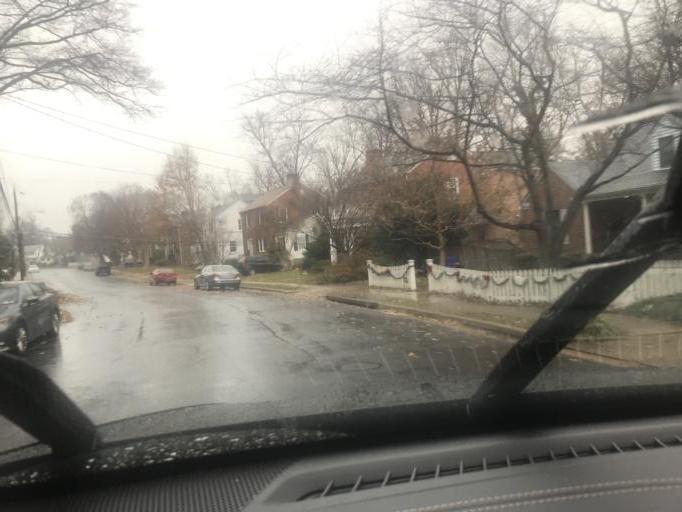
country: US
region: Virginia
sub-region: City of Alexandria
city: Alexandria
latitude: 38.8492
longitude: -77.0561
